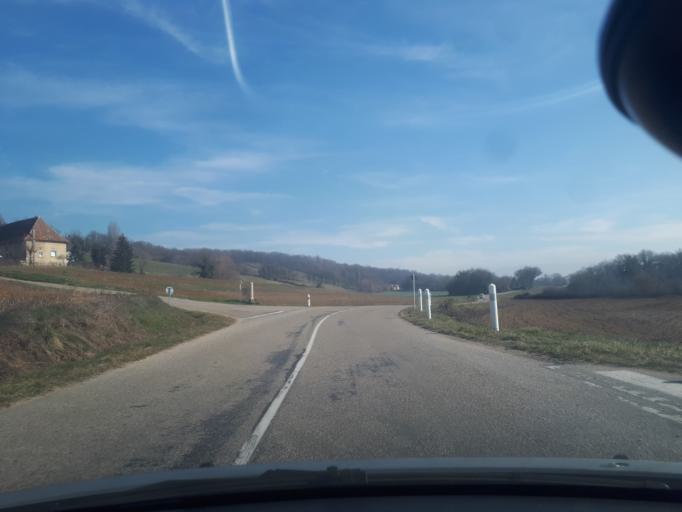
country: FR
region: Rhone-Alpes
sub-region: Departement de l'Isere
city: Sermerieu
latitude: 45.6682
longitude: 5.4213
